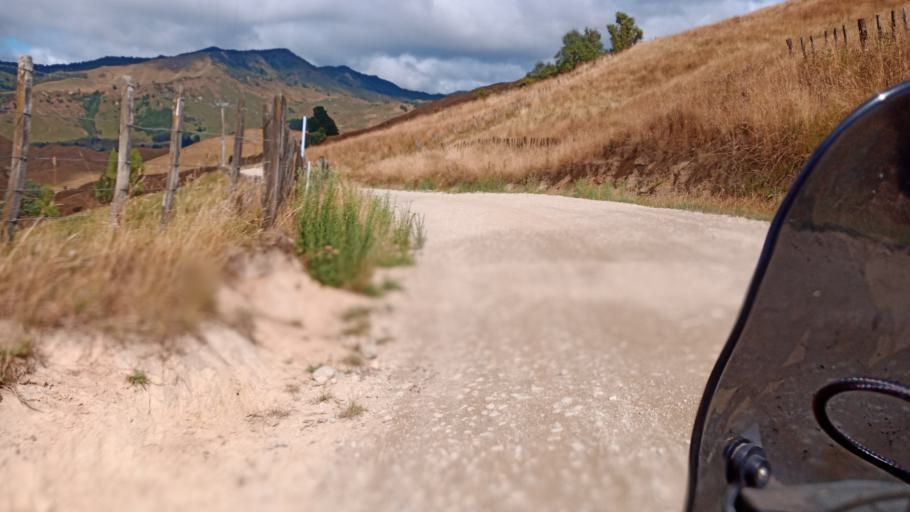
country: NZ
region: Hawke's Bay
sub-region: Wairoa District
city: Wairoa
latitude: -38.6102
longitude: 177.4430
